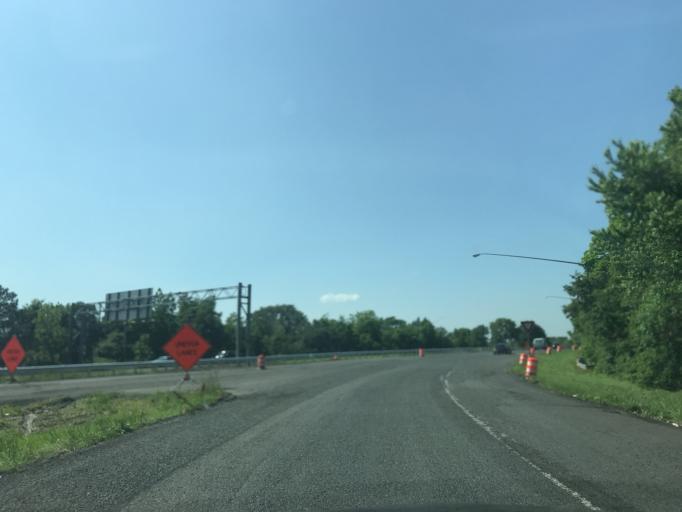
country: US
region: Maryland
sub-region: Wicomico County
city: Salisbury
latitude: 38.3725
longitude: -75.5375
